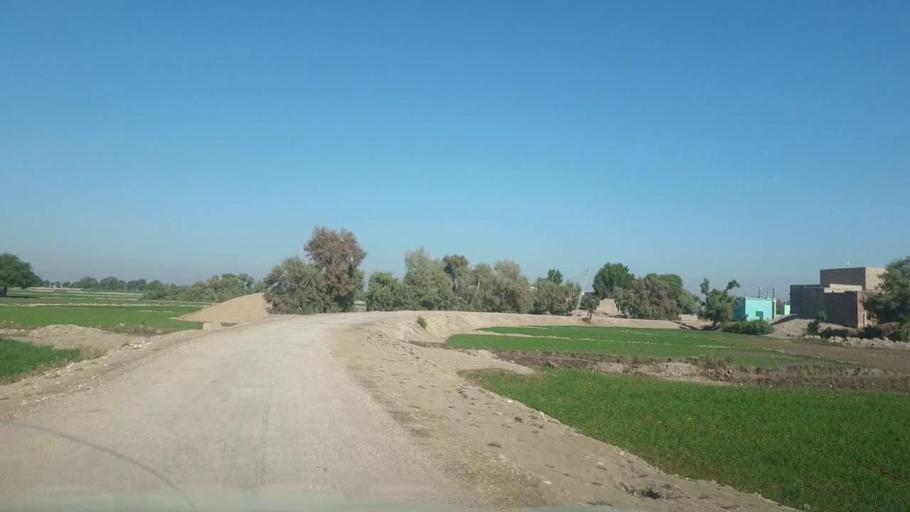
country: PK
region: Sindh
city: Bhan
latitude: 26.5242
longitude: 67.6424
